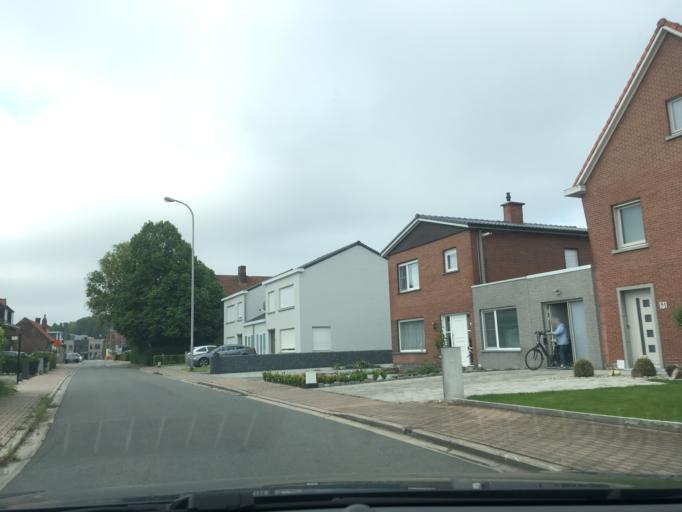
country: BE
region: Flanders
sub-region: Provincie West-Vlaanderen
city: Ingelmunster
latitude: 50.9243
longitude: 3.2491
